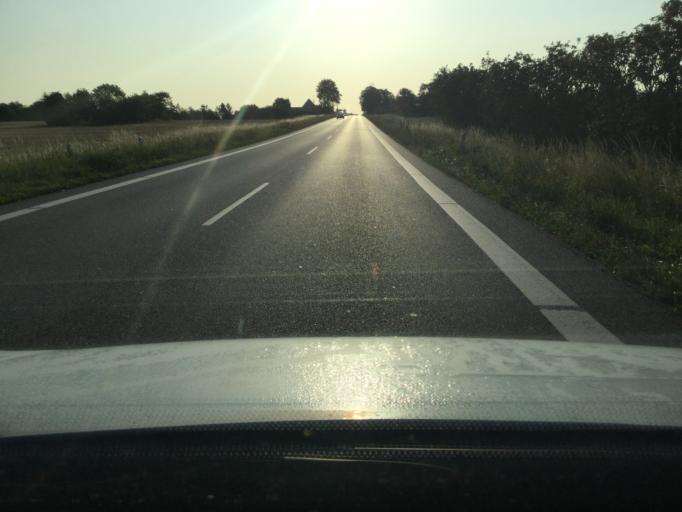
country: DK
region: Zealand
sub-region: Lolland Kommune
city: Nakskov
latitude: 54.8026
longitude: 11.2546
